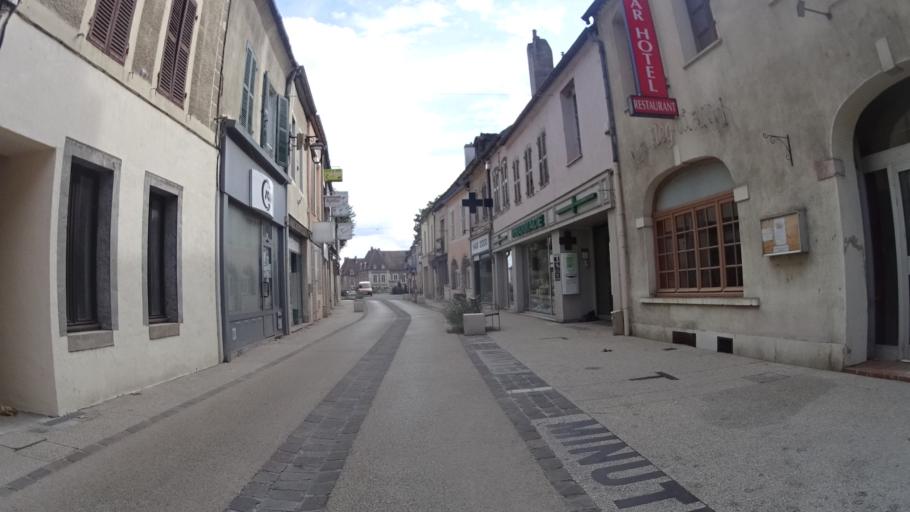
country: FR
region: Bourgogne
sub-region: Departement de la Cote-d'Or
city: Seurre
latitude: 46.9979
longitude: 5.1470
